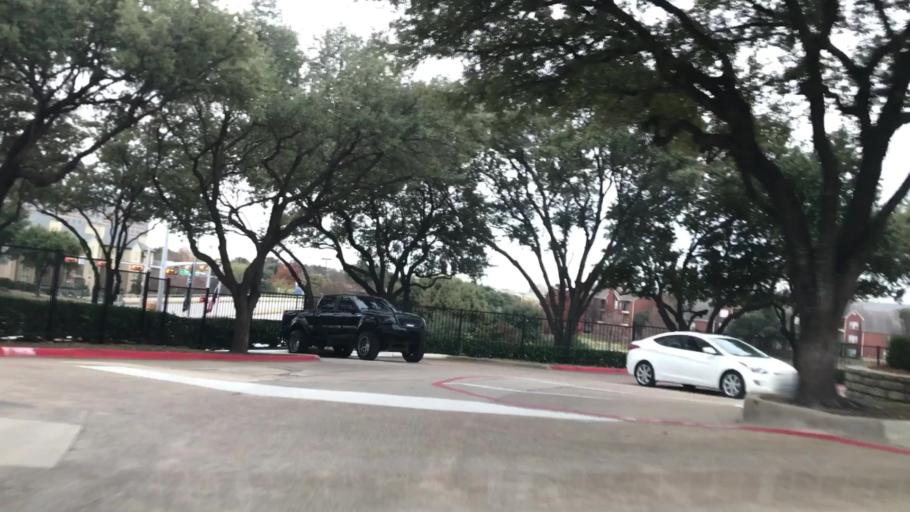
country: US
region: Texas
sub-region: Dallas County
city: Irving
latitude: 32.8809
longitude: -96.9640
